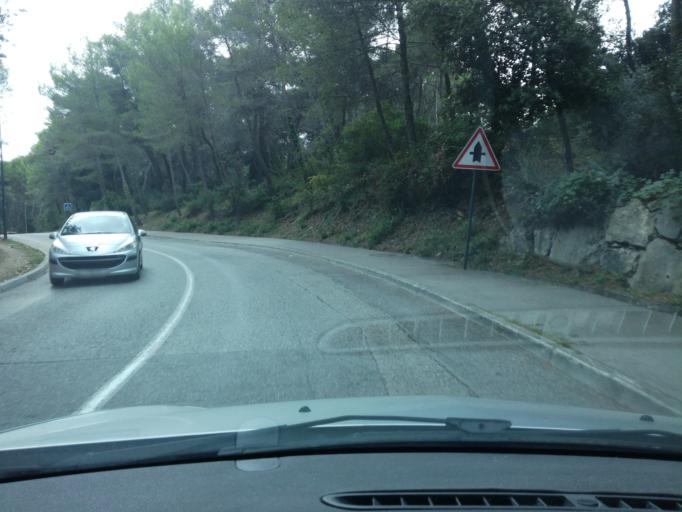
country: FR
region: Provence-Alpes-Cote d'Azur
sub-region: Departement des Alpes-Maritimes
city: Vallauris
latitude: 43.6150
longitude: 7.0531
